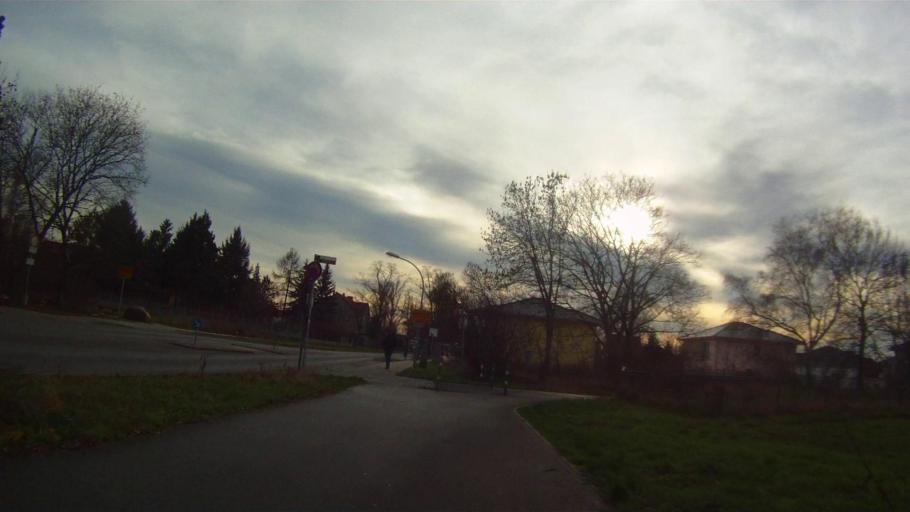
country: DE
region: Berlin
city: Buckow
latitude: 52.4147
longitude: 13.4386
